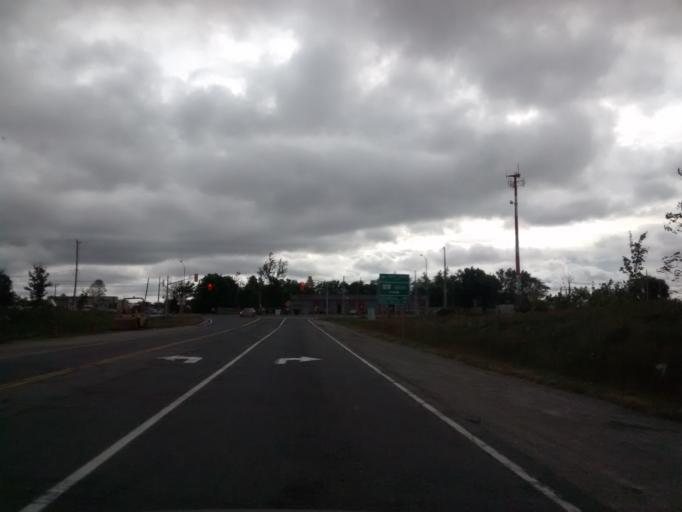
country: CA
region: Ontario
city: Ancaster
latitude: 43.1418
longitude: -79.9228
